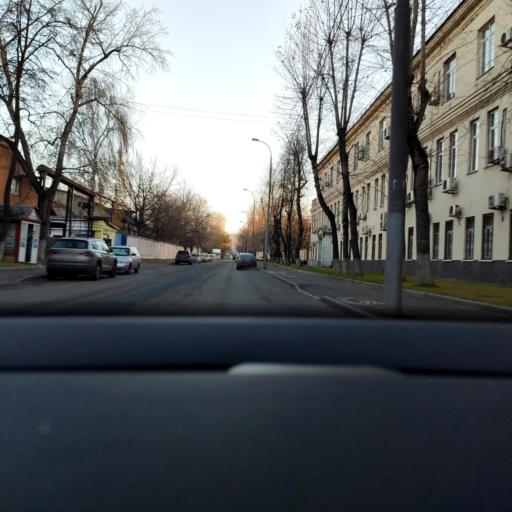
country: RU
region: Moscow
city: Ryazanskiy
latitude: 55.7210
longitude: 37.7549
